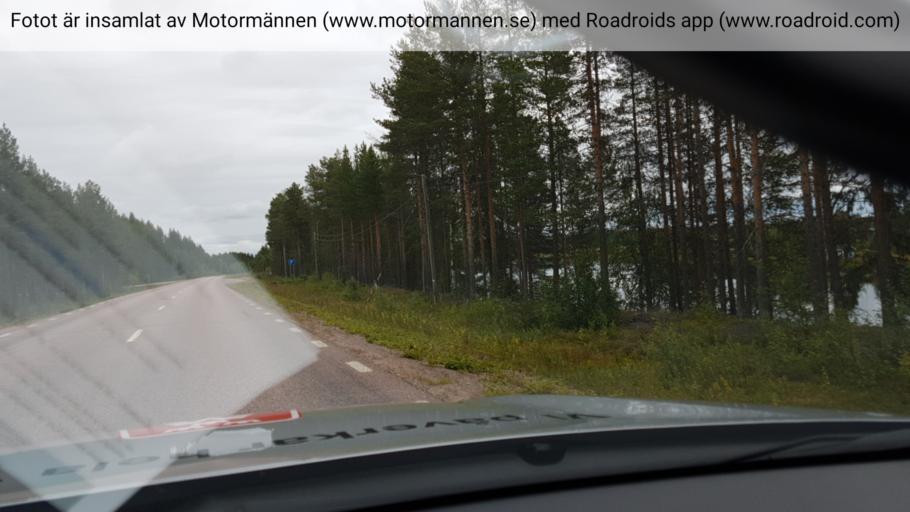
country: SE
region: Norrbotten
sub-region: Overkalix Kommun
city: OEverkalix
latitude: 67.0747
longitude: 22.5279
